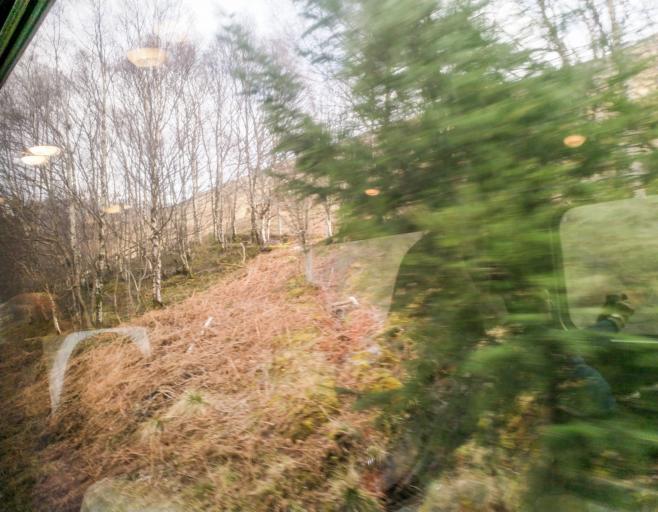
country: GB
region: Scotland
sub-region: Highland
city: Spean Bridge
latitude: 56.8034
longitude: -4.7196
